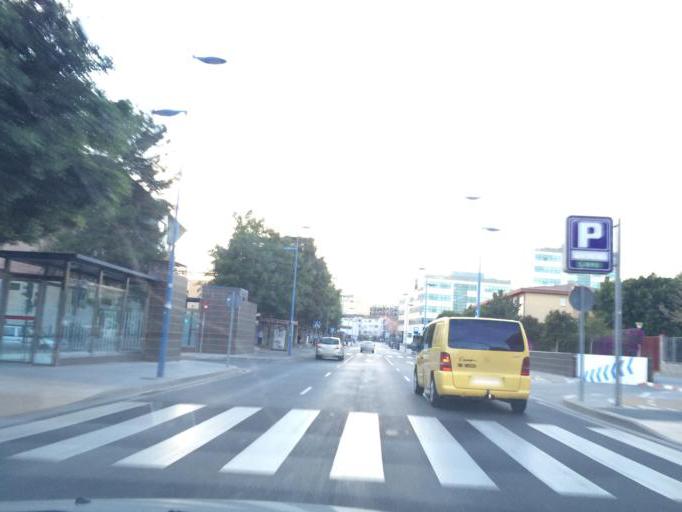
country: ES
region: Andalusia
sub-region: Provincia de Almeria
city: Almeria
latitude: 36.8395
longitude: -2.4511
